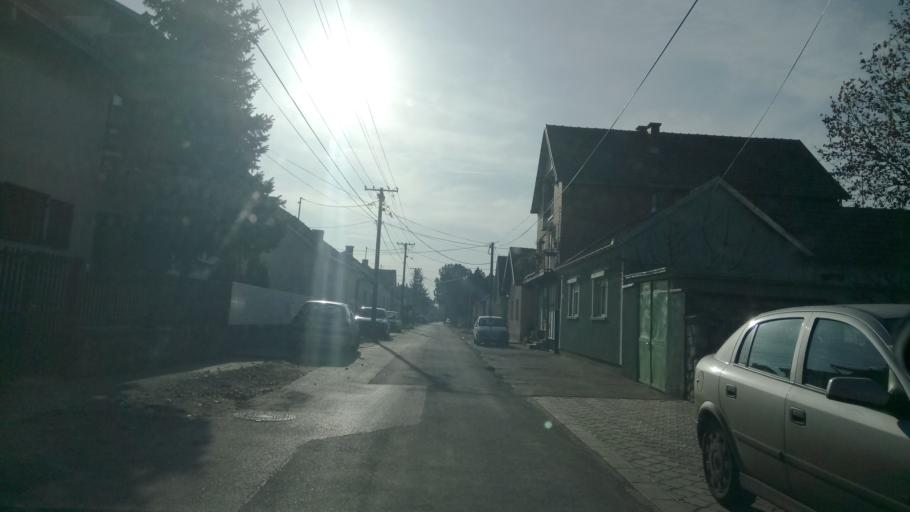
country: RS
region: Autonomna Pokrajina Vojvodina
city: Nova Pazova
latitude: 44.9501
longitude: 20.2227
